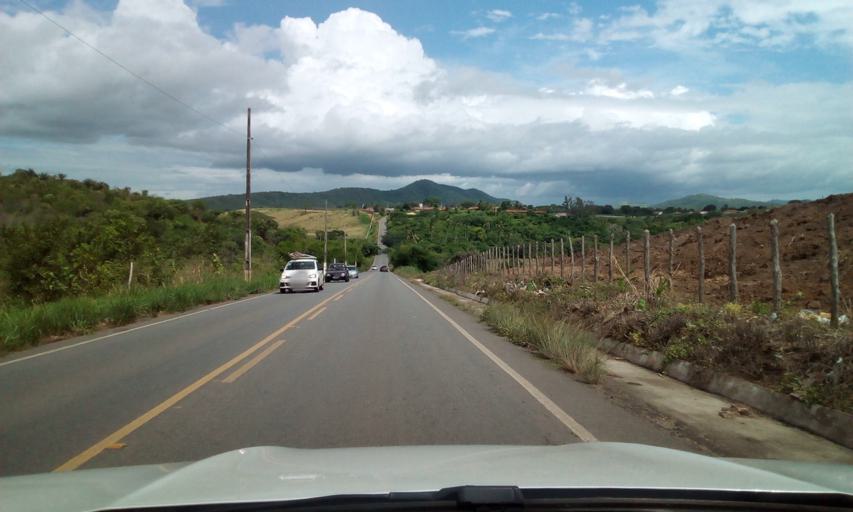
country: BR
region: Paraiba
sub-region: Guarabira
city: Guarabira
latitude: -6.8745
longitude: -35.5002
